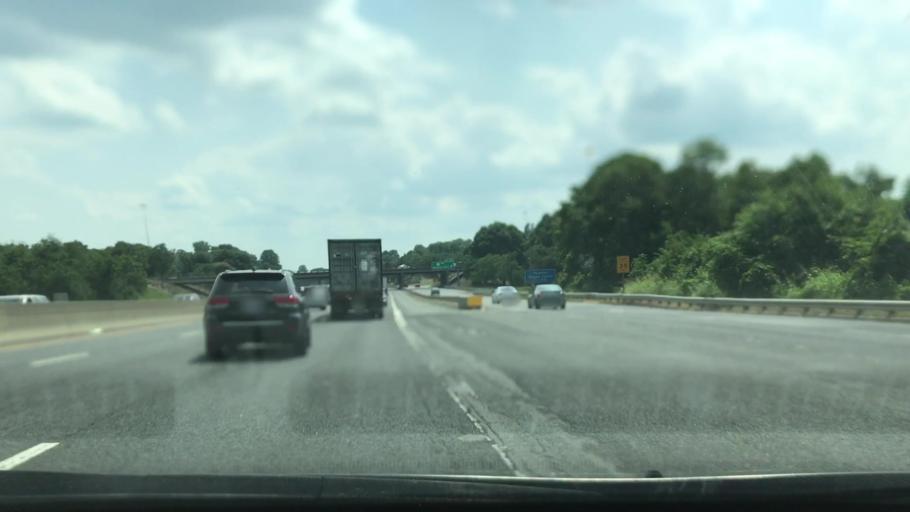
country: US
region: North Carolina
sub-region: Mecklenburg County
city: Charlotte
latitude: 35.2270
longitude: -80.8624
